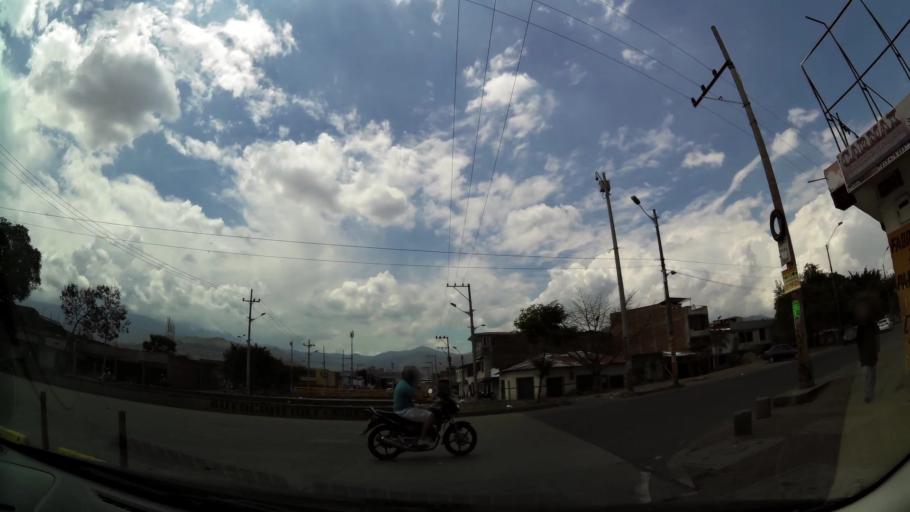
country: CO
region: Valle del Cauca
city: Cali
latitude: 3.4385
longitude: -76.5188
